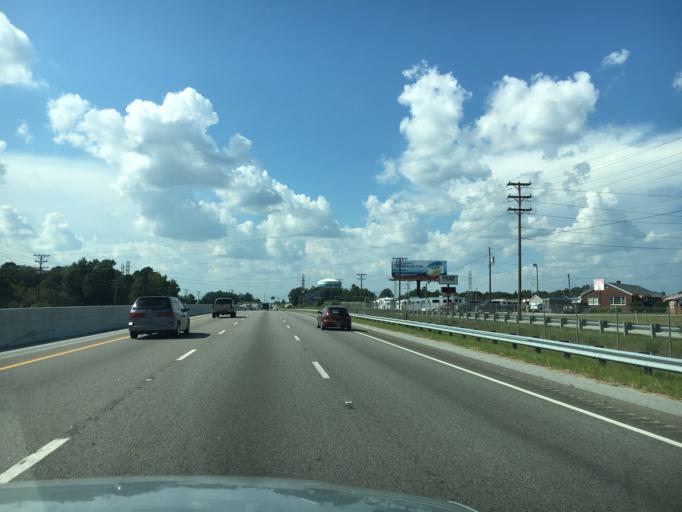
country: US
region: South Carolina
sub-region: Greenville County
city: Fountain Inn
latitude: 34.6903
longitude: -82.2211
